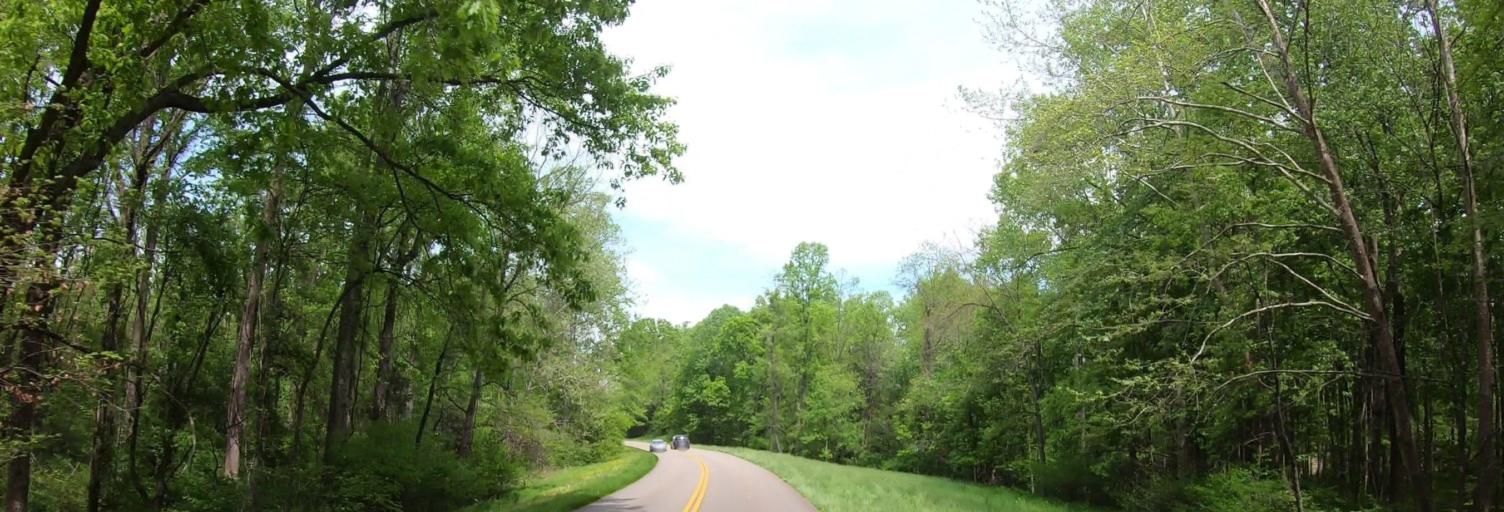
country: US
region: Virginia
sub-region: Roanoke County
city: Vinton
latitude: 37.2617
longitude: -79.8591
